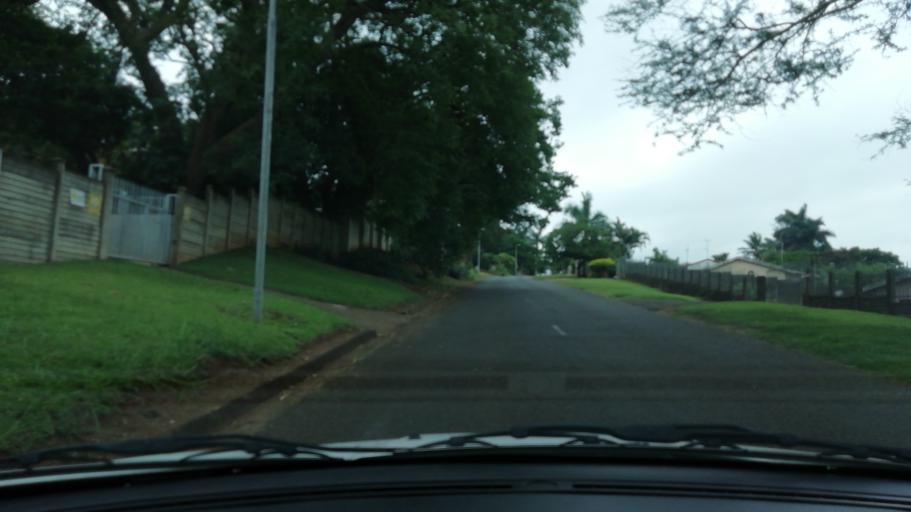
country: ZA
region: KwaZulu-Natal
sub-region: uThungulu District Municipality
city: Empangeni
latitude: -28.7381
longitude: 31.9024
